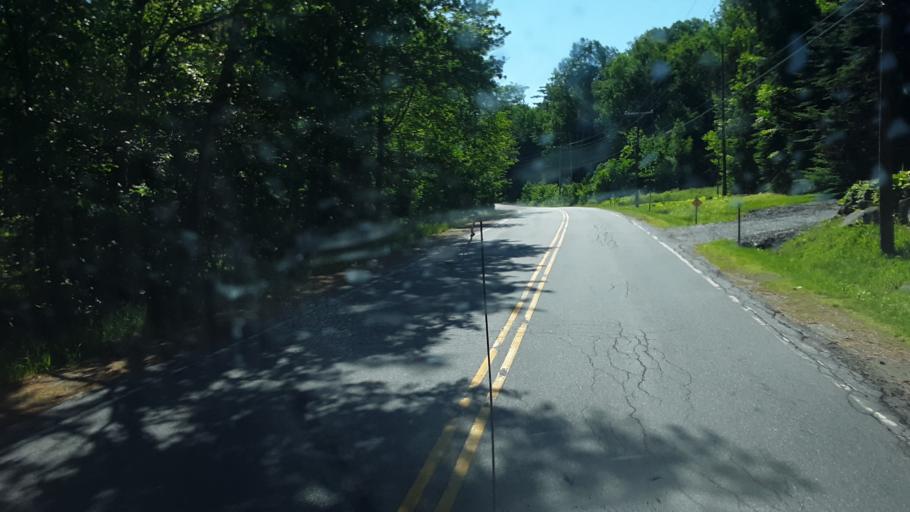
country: US
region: New Hampshire
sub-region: Grafton County
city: North Haverhill
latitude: 44.0995
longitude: -71.9219
